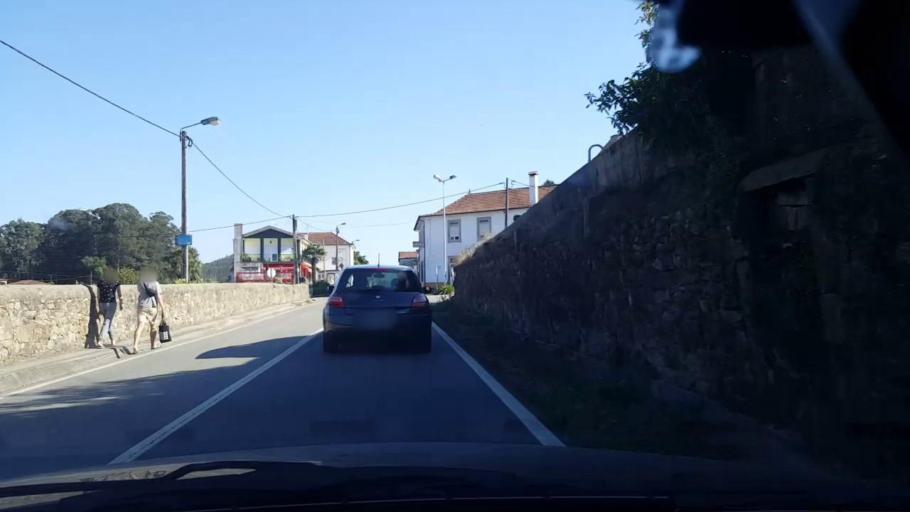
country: PT
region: Porto
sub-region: Vila do Conde
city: Arvore
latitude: 41.3324
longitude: -8.6639
